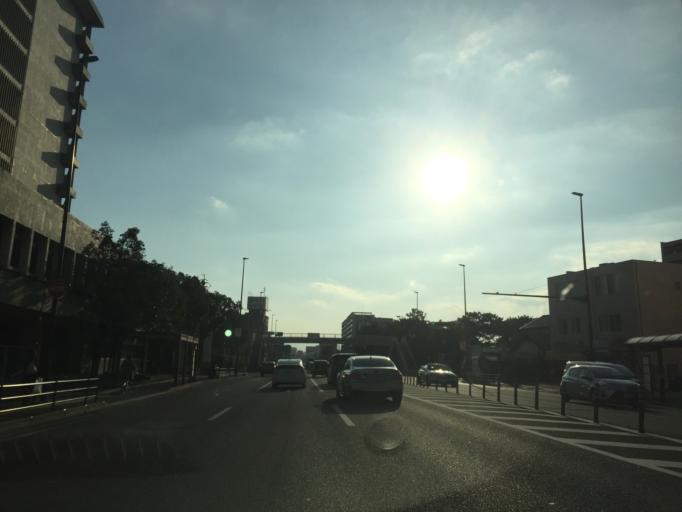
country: JP
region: Fukuoka
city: Fukuoka-shi
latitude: 33.6184
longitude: 130.4172
